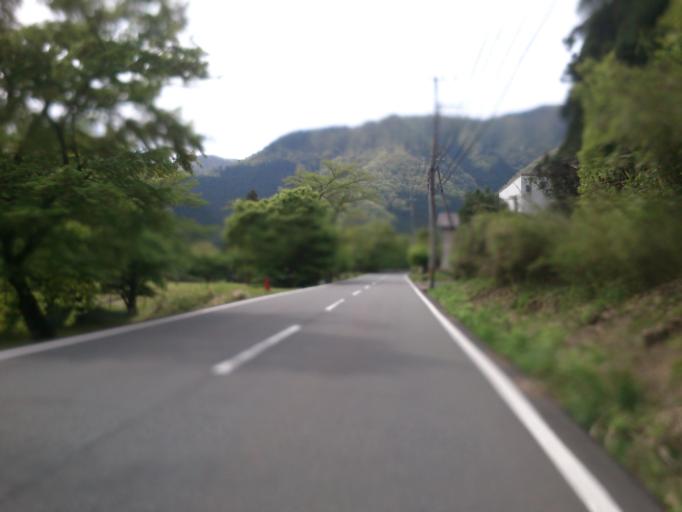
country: JP
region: Kyoto
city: Ayabe
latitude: 35.2718
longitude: 135.4665
